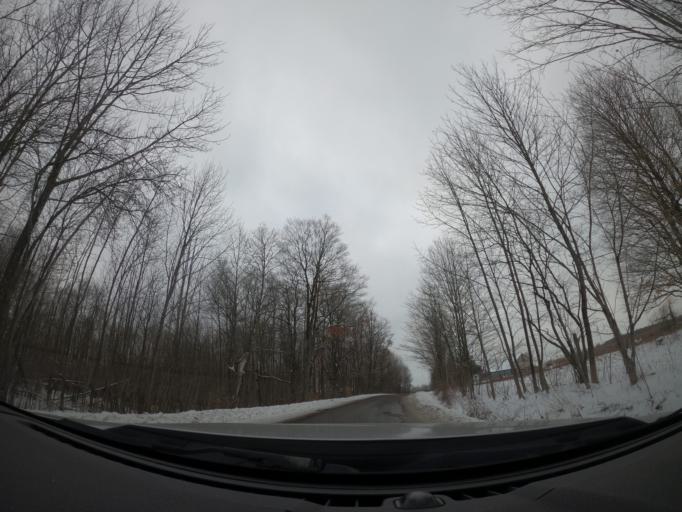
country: US
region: New York
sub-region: Cayuga County
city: Moravia
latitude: 42.7339
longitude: -76.3054
